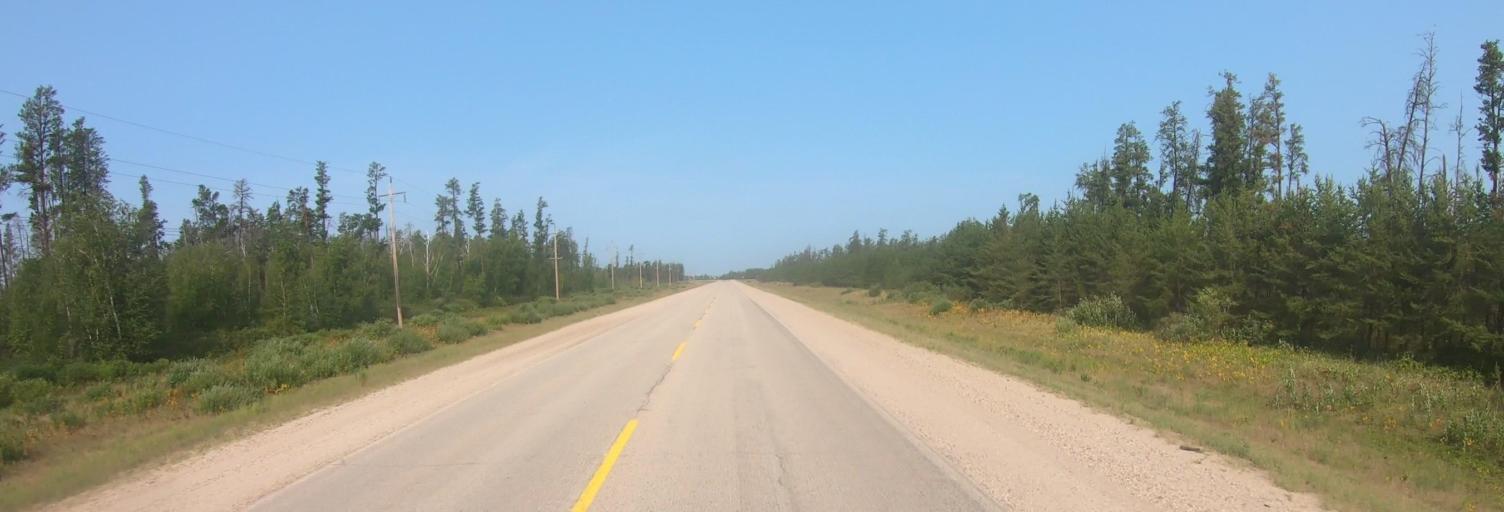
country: US
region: Minnesota
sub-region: Roseau County
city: Roseau
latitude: 49.0848
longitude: -95.8801
